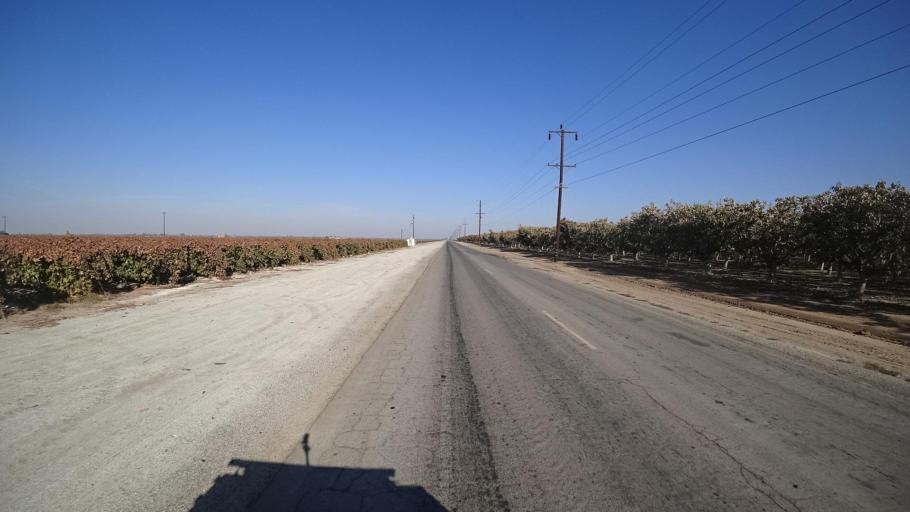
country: US
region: California
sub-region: Kern County
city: McFarland
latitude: 35.7277
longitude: -119.2051
